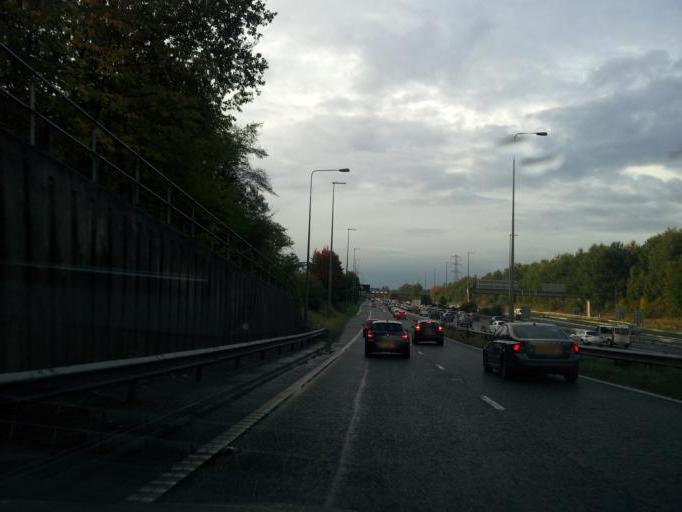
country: GB
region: England
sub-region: Manchester
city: Crumpsall
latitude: 53.5405
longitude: -2.2398
